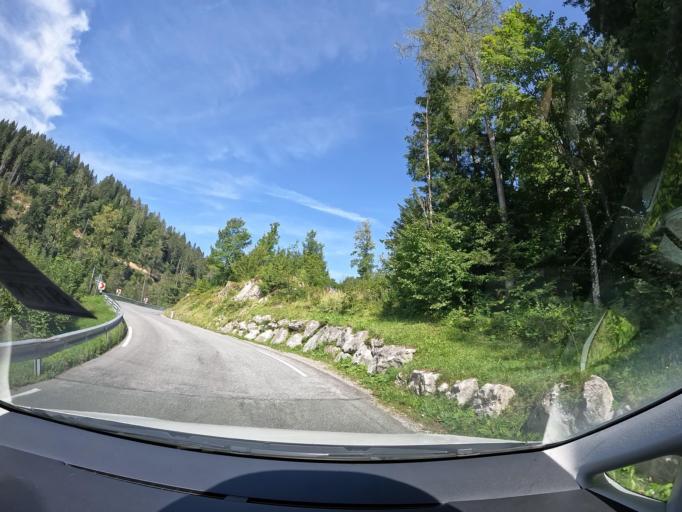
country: AT
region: Carinthia
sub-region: Politischer Bezirk Klagenfurt Land
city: Schiefling am See
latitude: 46.5826
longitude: 14.0769
